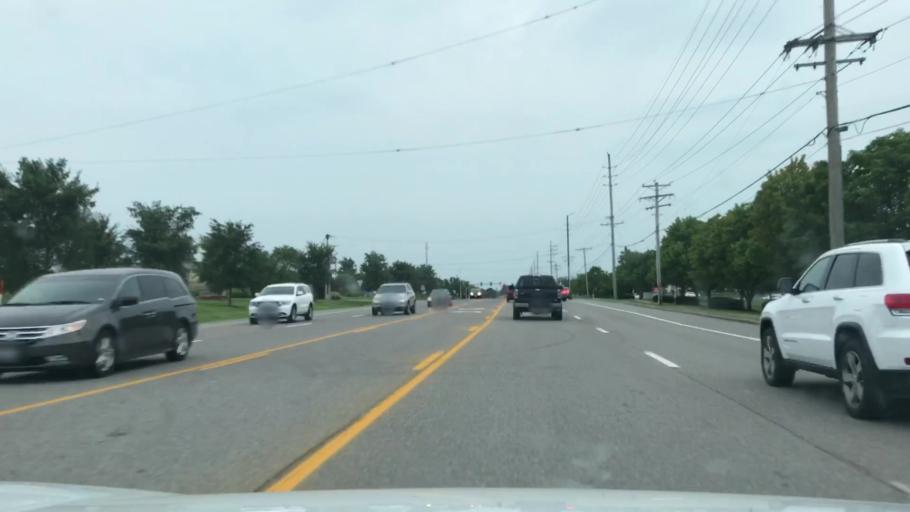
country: US
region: Missouri
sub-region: Saint Louis County
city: Clarkson Valley
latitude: 38.6077
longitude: -90.5858
